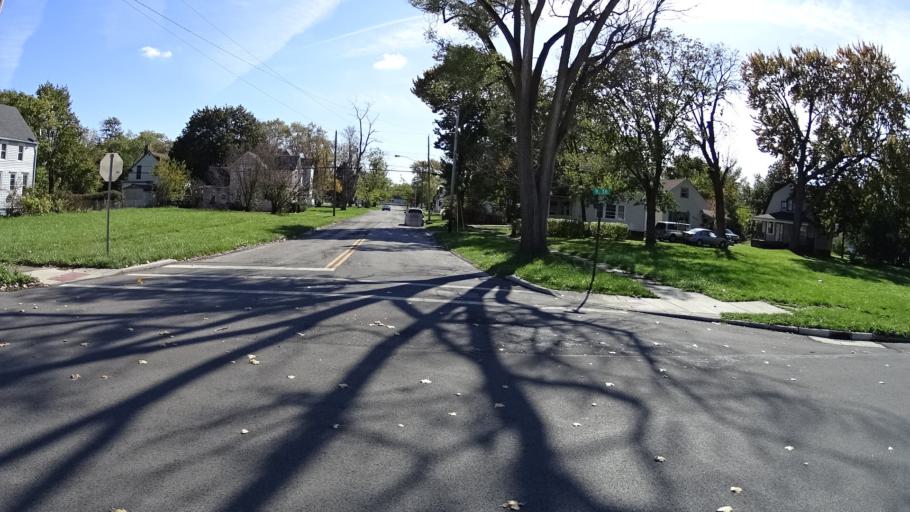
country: US
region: Ohio
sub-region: Lorain County
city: Lorain
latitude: 41.4611
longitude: -82.1771
